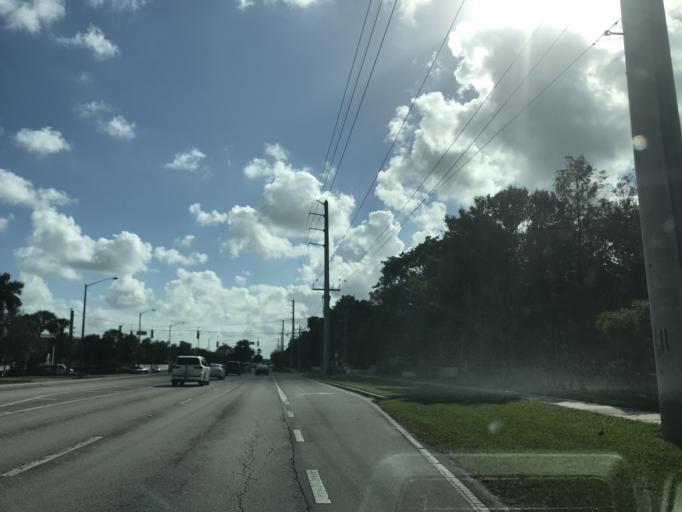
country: US
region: Florida
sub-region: Broward County
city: Coconut Creek
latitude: 26.2520
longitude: -80.1865
